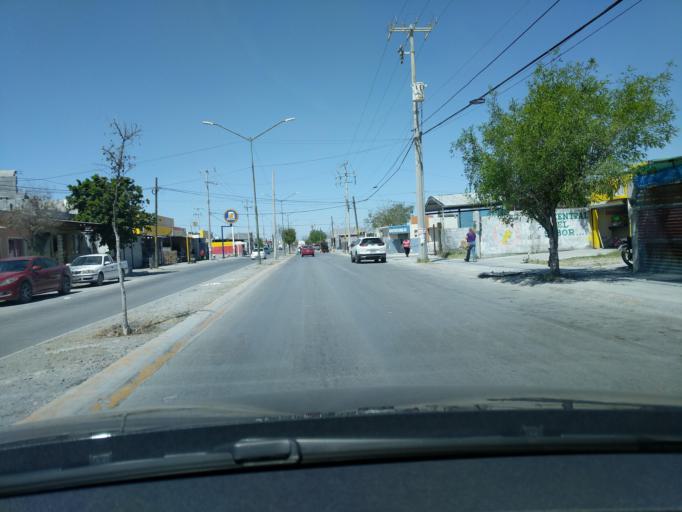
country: MX
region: Nuevo Leon
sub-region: Pesqueria
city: Colinas del Aeropuerto
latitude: 25.8222
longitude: -100.1091
